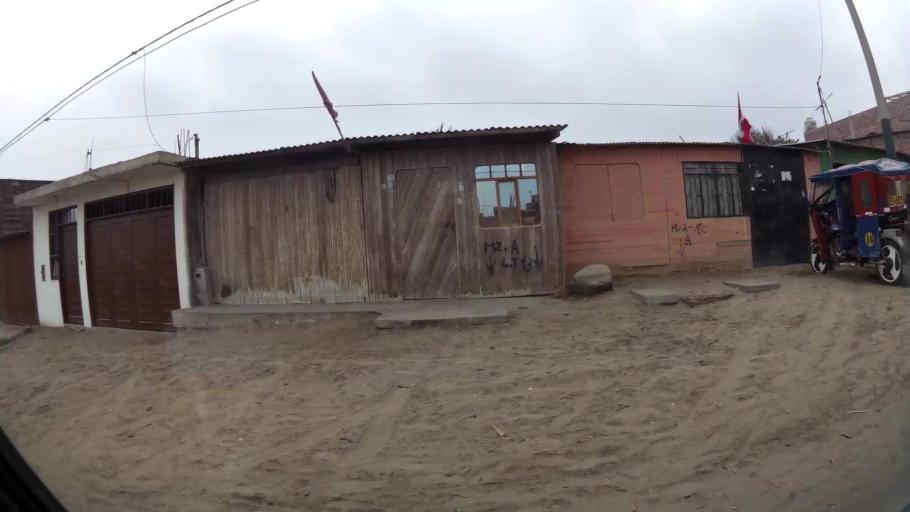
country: PE
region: Lima
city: Ventanilla
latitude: -11.8447
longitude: -77.1451
